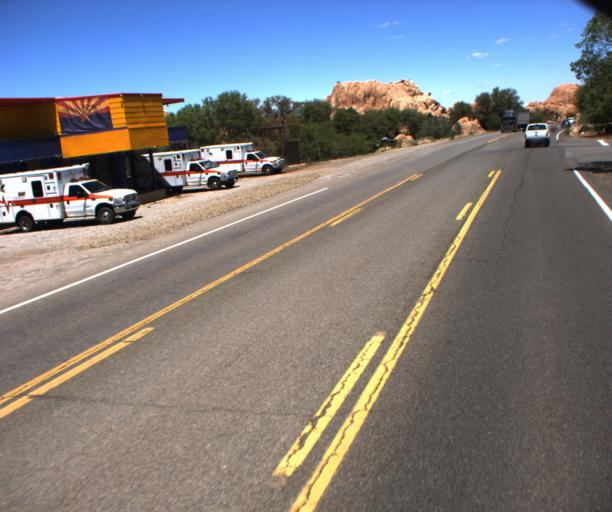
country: US
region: Arizona
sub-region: Yavapai County
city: Prescott
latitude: 34.6009
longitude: -112.4244
